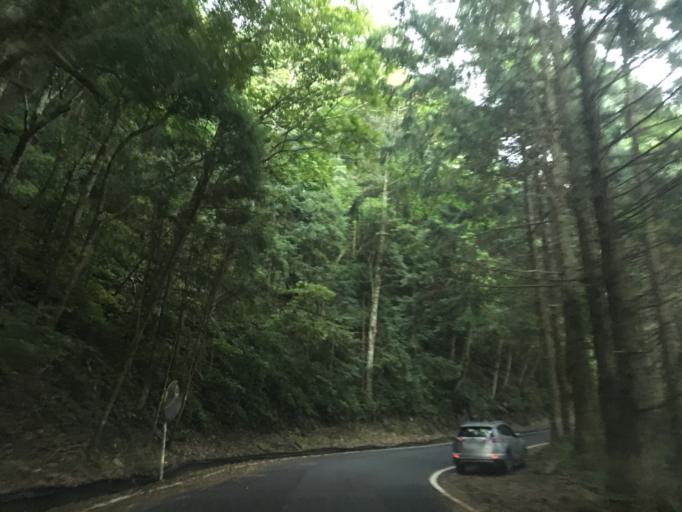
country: TW
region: Taiwan
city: Fengyuan
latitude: 24.2464
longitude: 120.9191
